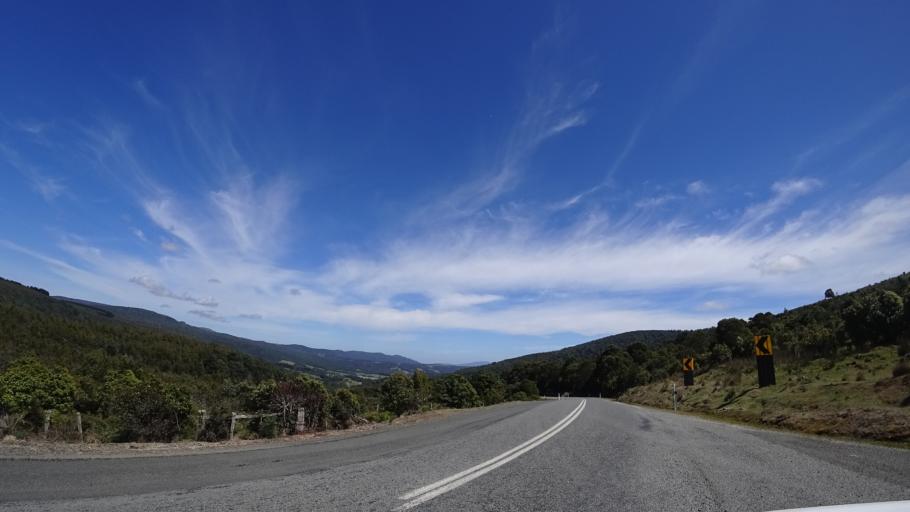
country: AU
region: Tasmania
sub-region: Break O'Day
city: St Helens
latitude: -41.2262
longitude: 147.9582
